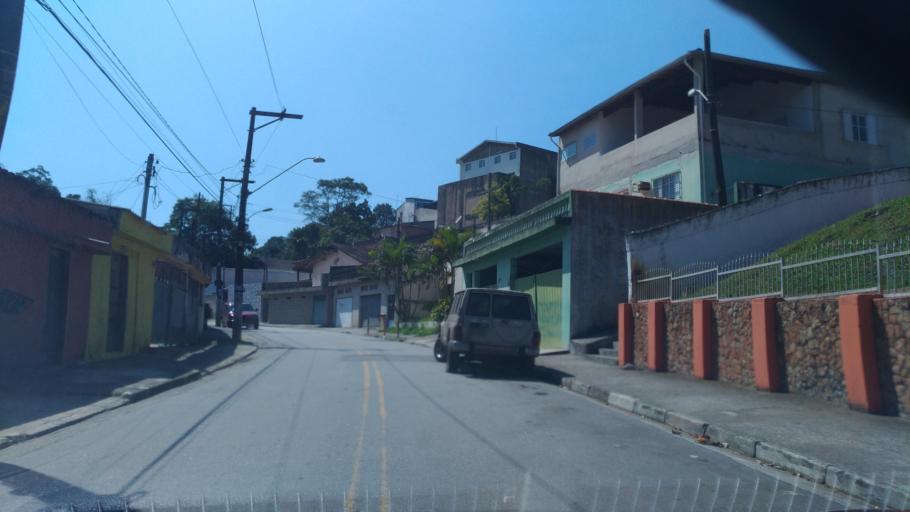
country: BR
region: Sao Paulo
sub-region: Sao Bernardo Do Campo
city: Sao Bernardo do Campo
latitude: -23.7757
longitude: -46.5190
